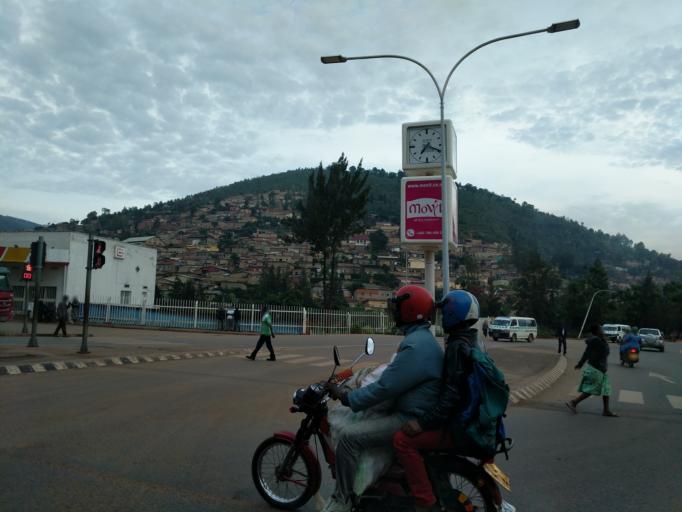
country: RW
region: Kigali
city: Kigali
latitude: -1.9428
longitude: 30.0420
